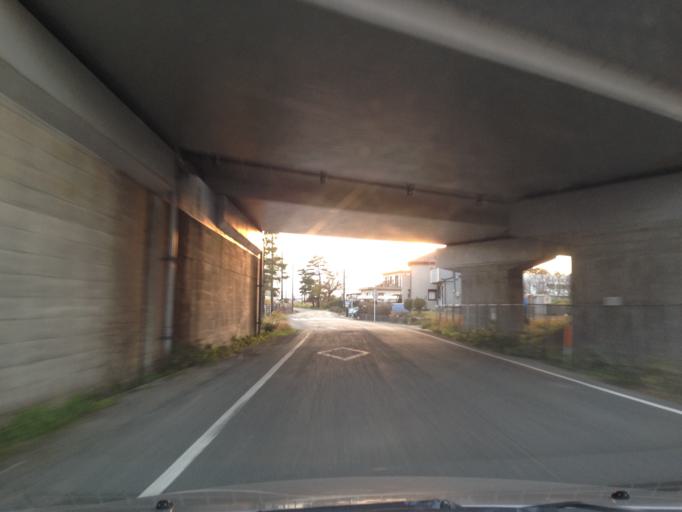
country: JP
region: Shizuoka
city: Kakegawa
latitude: 34.7679
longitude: 137.9742
